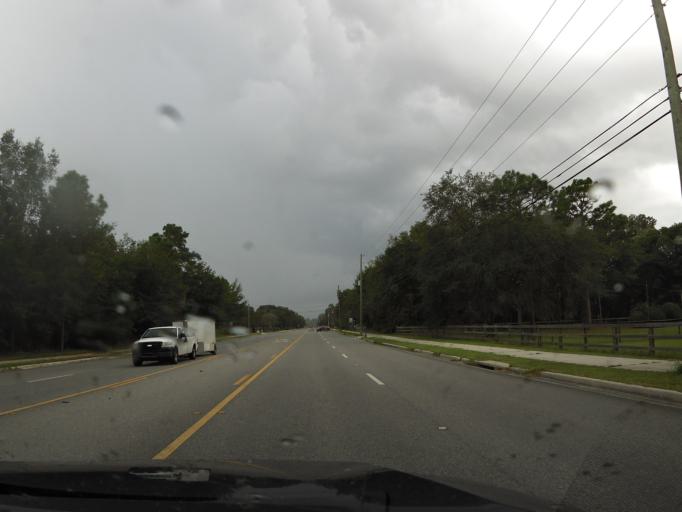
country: US
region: Florida
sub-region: Clay County
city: Asbury Lake
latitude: 30.0405
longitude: -81.8093
